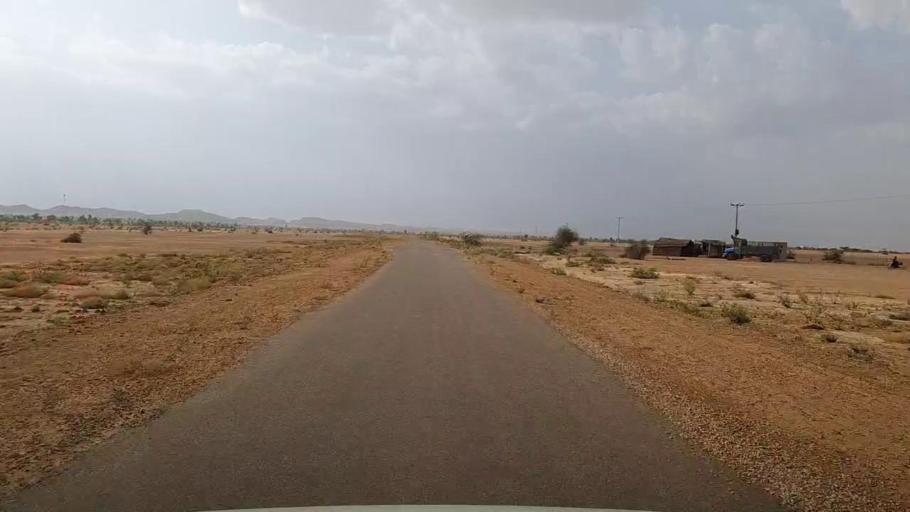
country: PK
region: Sindh
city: Jamshoro
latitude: 25.4719
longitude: 67.6756
